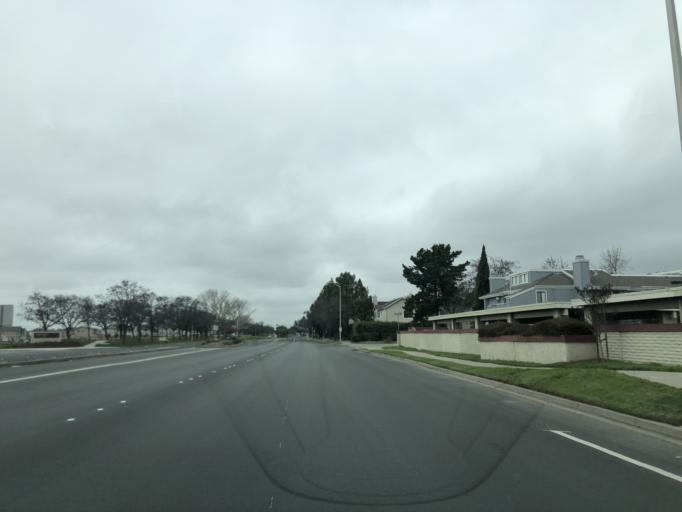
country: US
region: California
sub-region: Alameda County
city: Fremont
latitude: 37.5151
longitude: -121.9967
